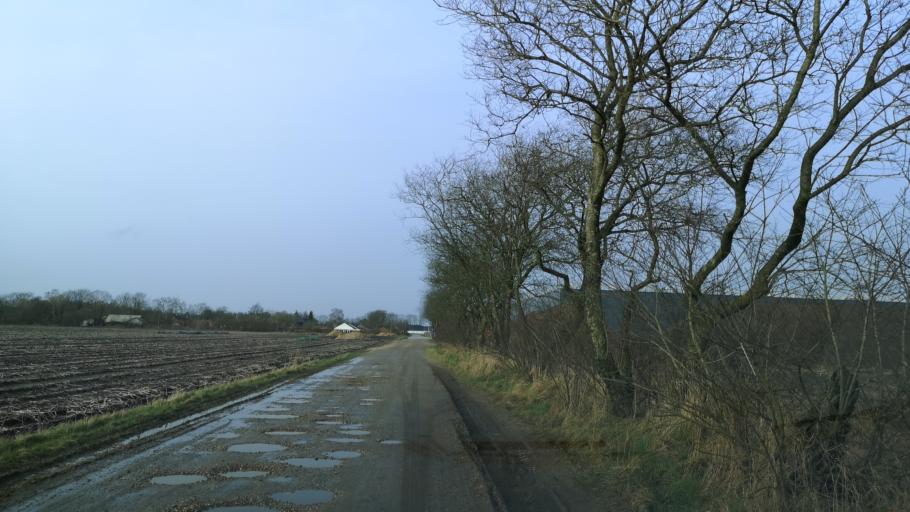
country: DK
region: Central Jutland
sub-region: Ikast-Brande Kommune
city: Brande
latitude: 56.0028
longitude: 9.1150
